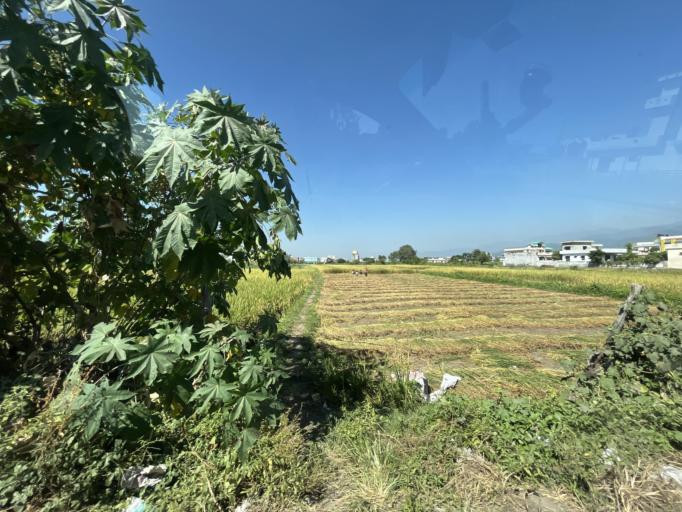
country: IN
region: Uttarakhand
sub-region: Naini Tal
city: Haldwani
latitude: 29.2095
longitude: 79.4943
